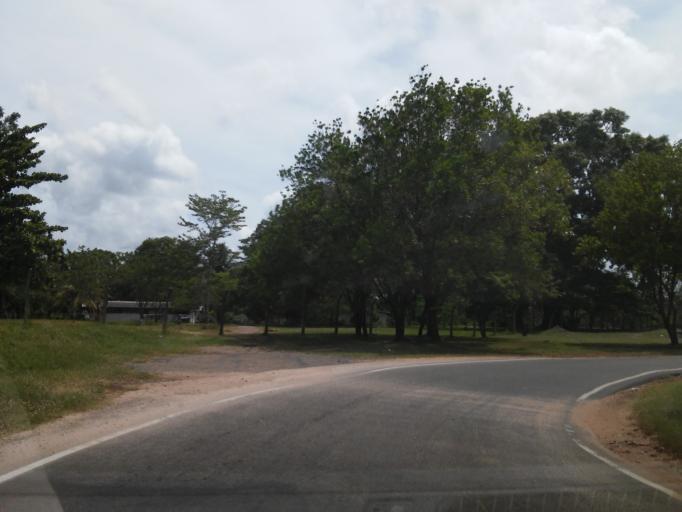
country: LK
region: North Central
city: Anuradhapura
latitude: 8.3470
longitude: 80.4003
